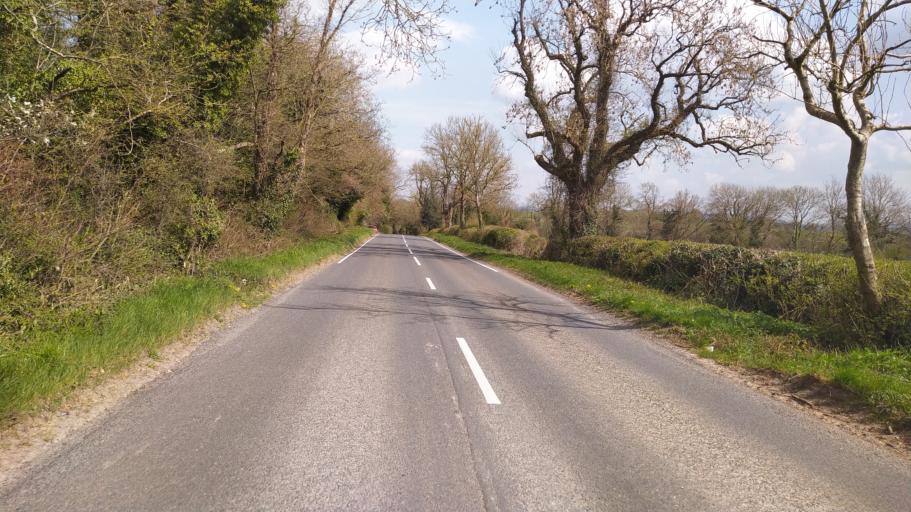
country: GB
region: England
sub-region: Somerset
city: Frome
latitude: 51.2349
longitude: -2.3738
